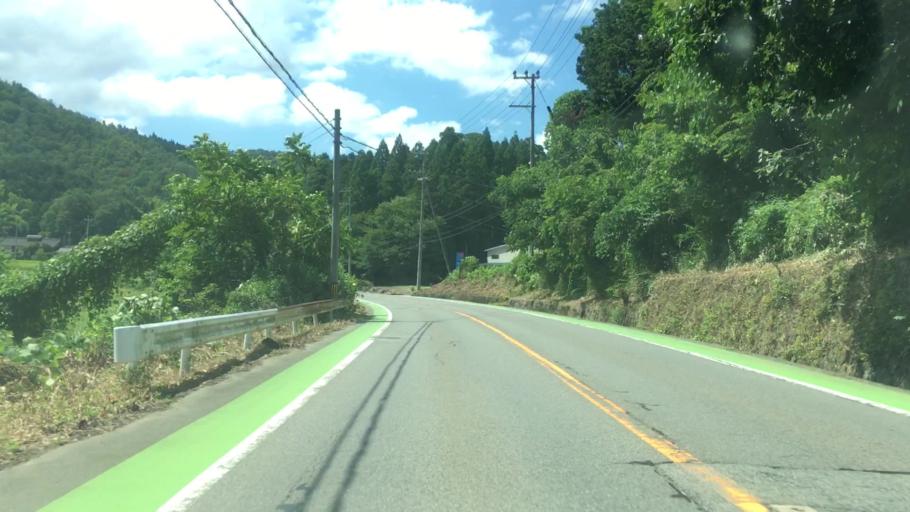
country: JP
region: Hyogo
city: Toyooka
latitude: 35.4759
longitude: 134.7117
